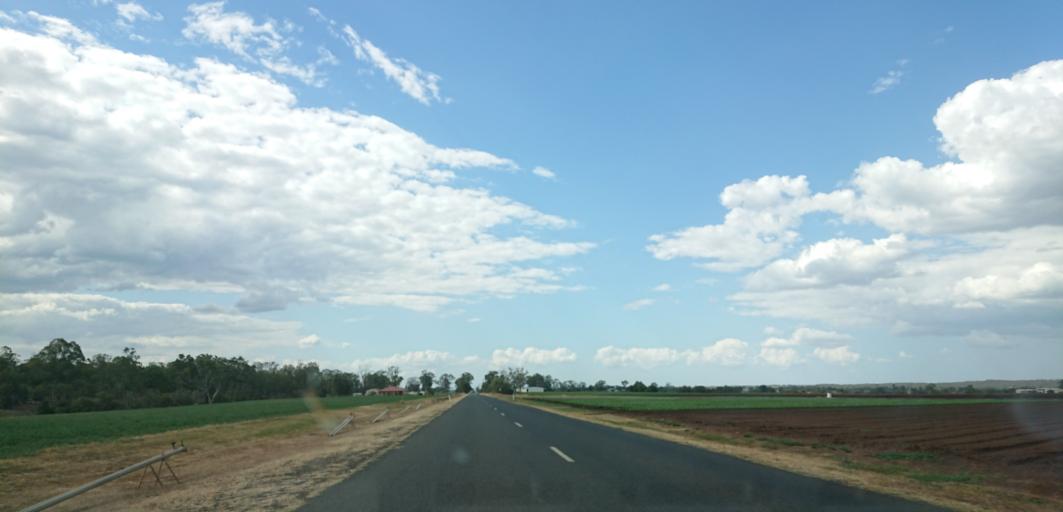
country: AU
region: Queensland
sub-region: Lockyer Valley
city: Gatton
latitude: -27.6045
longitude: 152.2134
